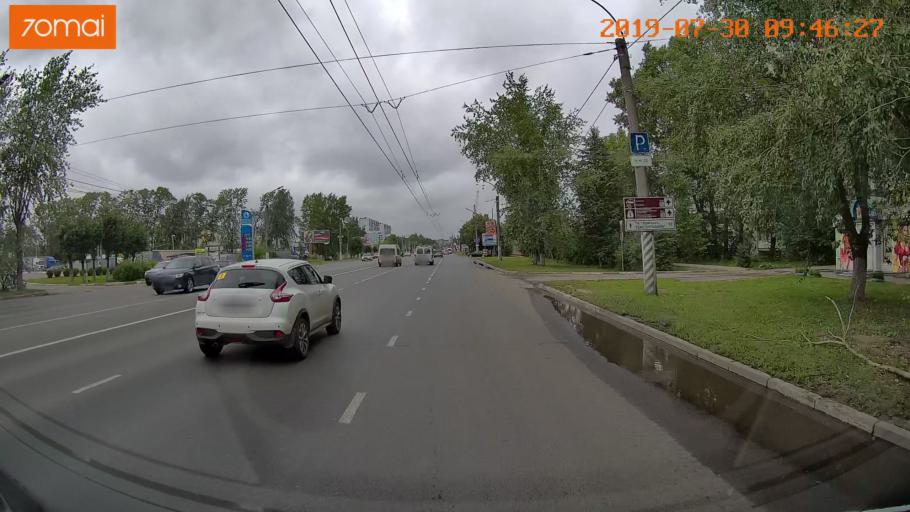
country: RU
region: Ivanovo
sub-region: Gorod Ivanovo
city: Ivanovo
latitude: 56.9555
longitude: 40.9747
